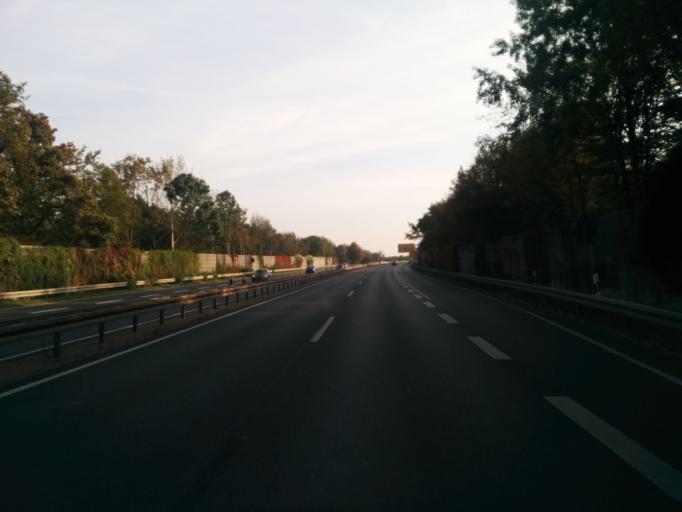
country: DE
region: Lower Saxony
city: Laatzen
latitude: 52.3482
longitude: 9.7881
